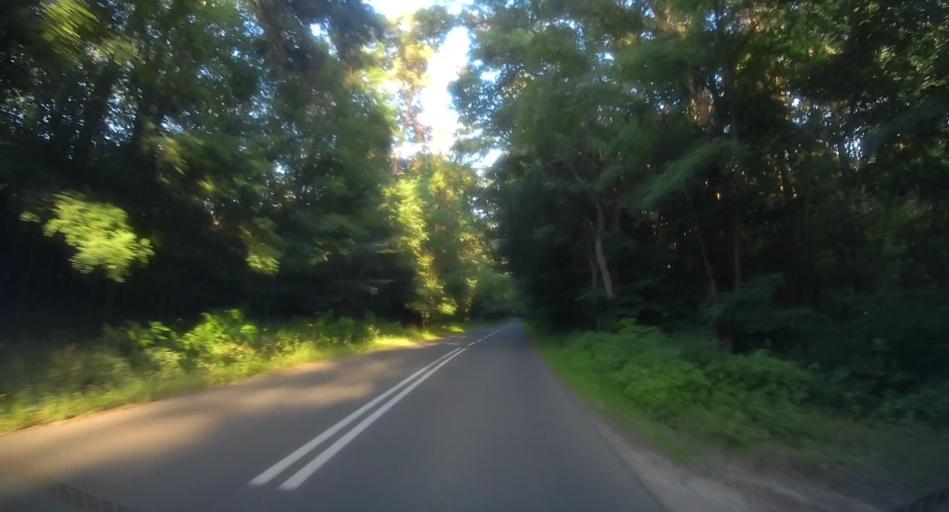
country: PL
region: Lodz Voivodeship
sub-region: Powiat skierniewicki
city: Kowiesy
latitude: 51.8912
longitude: 20.3950
